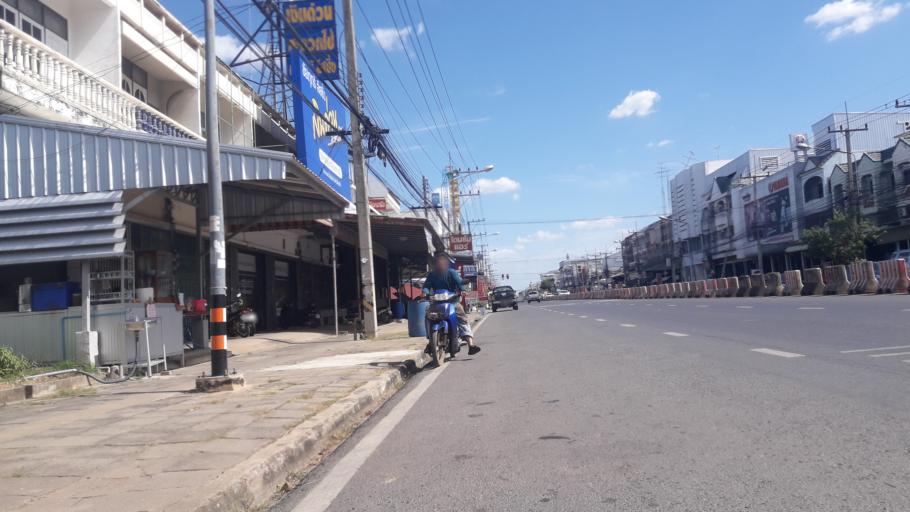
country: TH
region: Phichit
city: Thap Khlo
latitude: 16.1694
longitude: 100.5745
